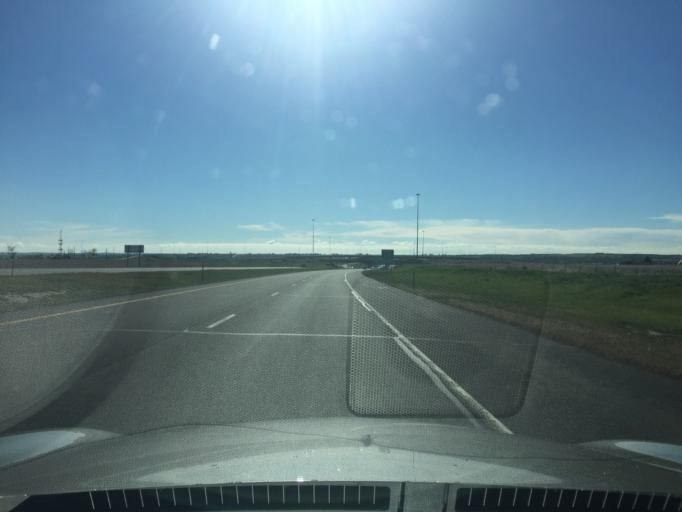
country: US
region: Colorado
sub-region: Boulder County
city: Erie
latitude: 39.9845
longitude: -105.0046
